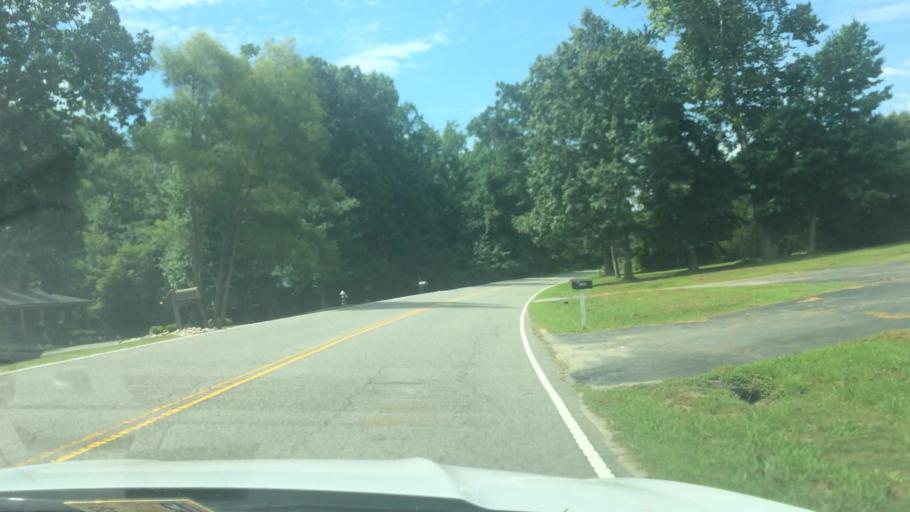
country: US
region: Virginia
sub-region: City of Poquoson
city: Poquoson
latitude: 37.1637
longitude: -76.4381
